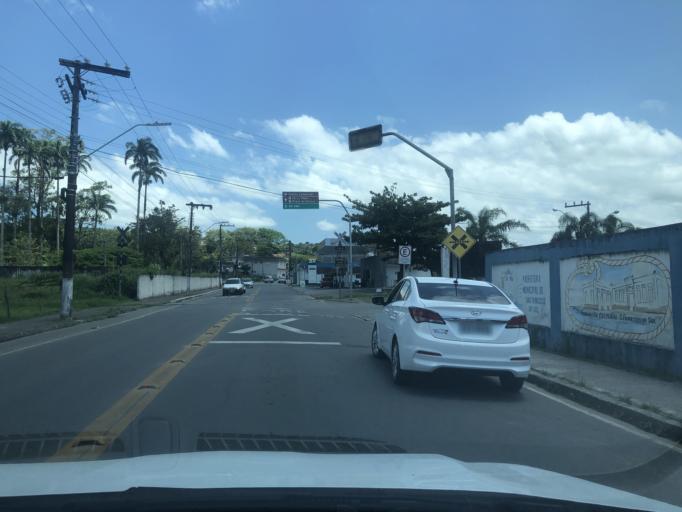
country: BR
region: Santa Catarina
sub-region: Sao Francisco Do Sul
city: Sao Francisco do Sul
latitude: -26.2502
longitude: -48.6415
